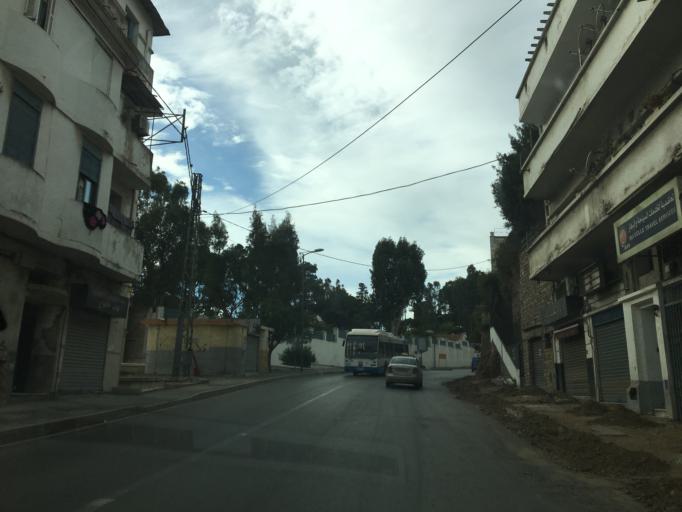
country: DZ
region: Alger
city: Algiers
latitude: 36.7719
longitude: 3.0409
